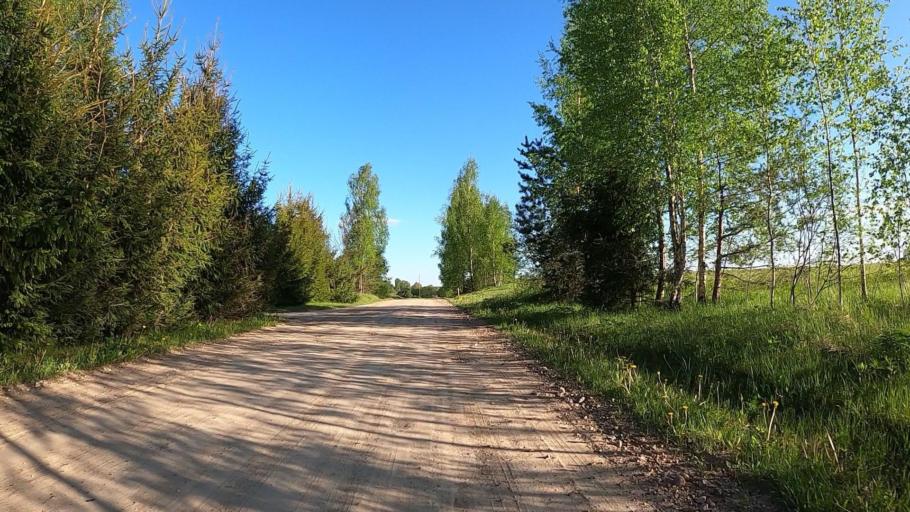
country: LV
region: Kekava
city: Kekava
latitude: 56.7721
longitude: 24.2871
